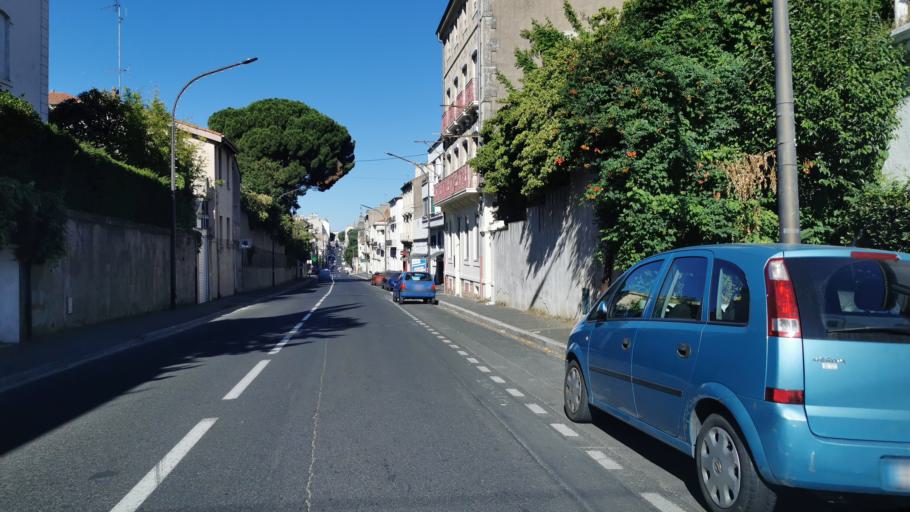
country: FR
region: Languedoc-Roussillon
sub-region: Departement de l'Herault
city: Beziers
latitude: 43.3439
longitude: 3.2268
